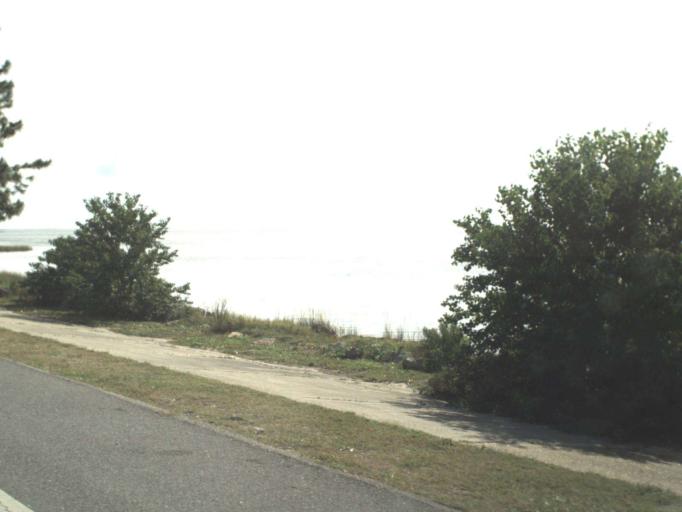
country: US
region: Florida
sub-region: Gulf County
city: Port Saint Joe
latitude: 29.8034
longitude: -85.3017
